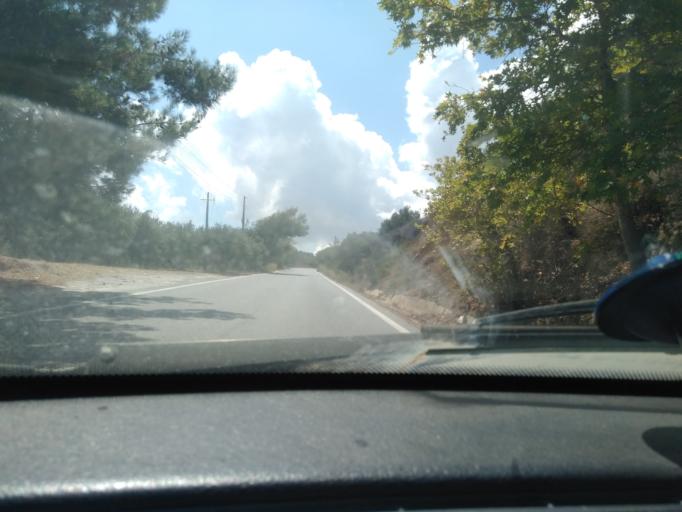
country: GR
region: Crete
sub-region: Nomos Lasithiou
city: Siteia
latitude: 35.1274
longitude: 26.0661
